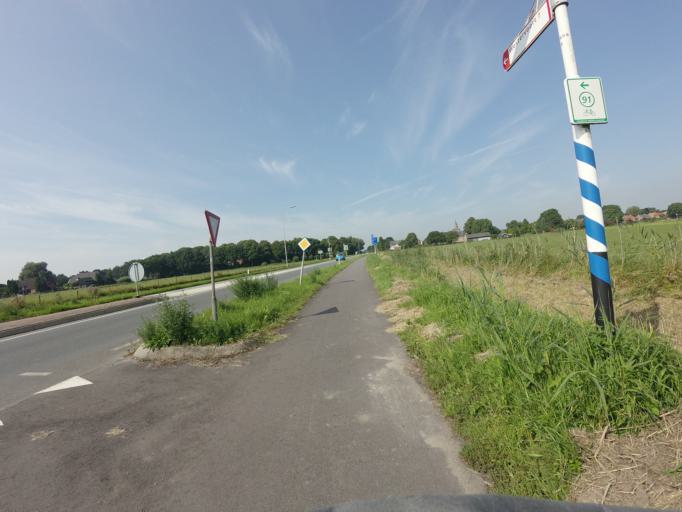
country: NL
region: Gelderland
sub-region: Gemeente Rheden
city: Rheden
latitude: 51.9854
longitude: 6.0254
